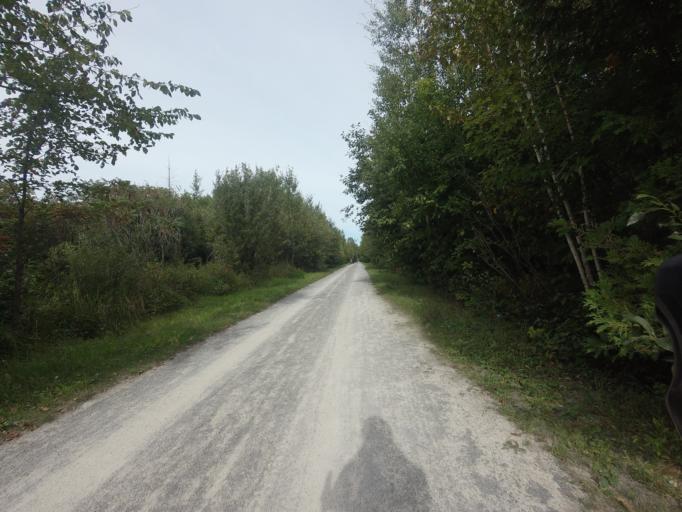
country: CA
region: Ontario
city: Bells Corners
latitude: 45.2474
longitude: -75.9382
